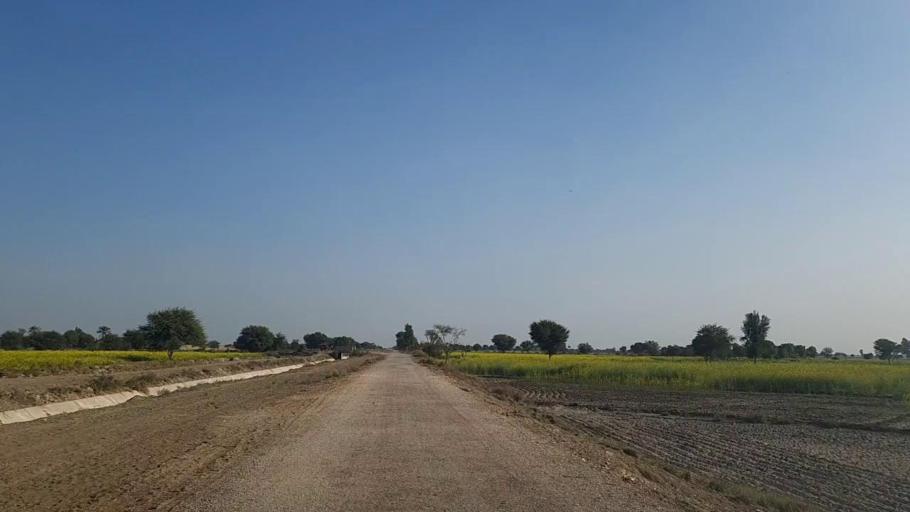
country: PK
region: Sindh
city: Shahpur Chakar
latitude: 26.2026
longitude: 68.6467
